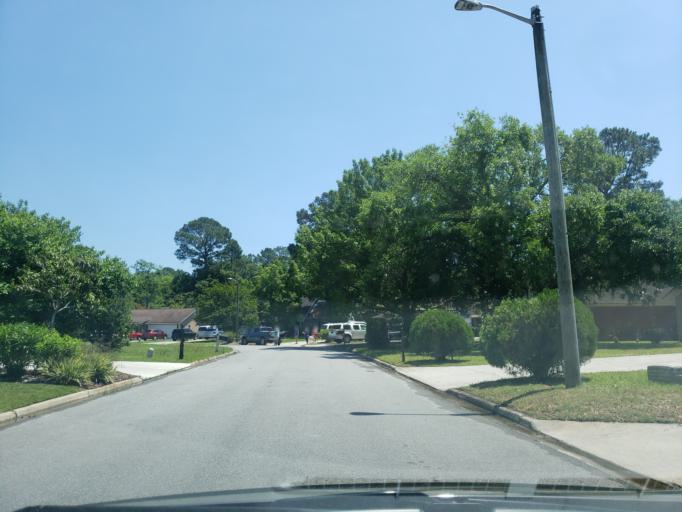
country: US
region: Georgia
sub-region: Chatham County
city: Isle of Hope
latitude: 31.9782
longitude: -81.0826
